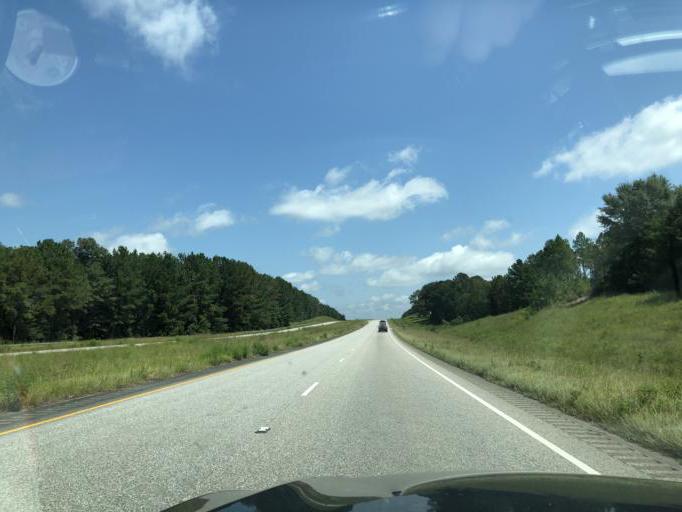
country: US
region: Alabama
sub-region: Barbour County
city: Eufaula
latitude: 31.7454
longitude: -85.2378
